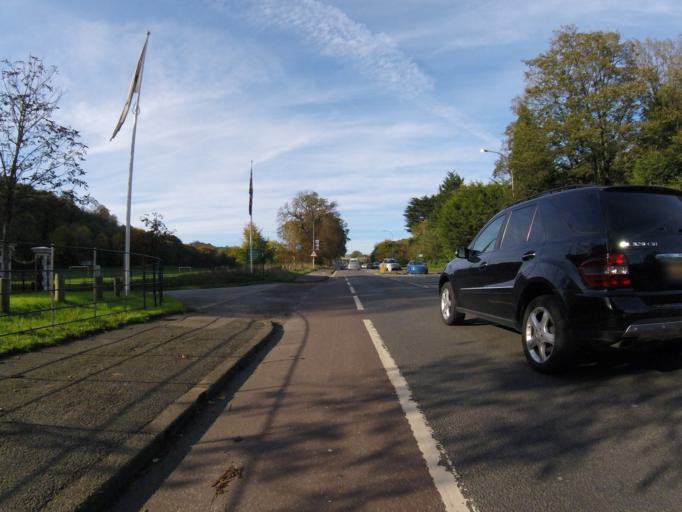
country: GB
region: England
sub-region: Brighton and Hove
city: Hove
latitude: 50.8655
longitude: -0.1530
